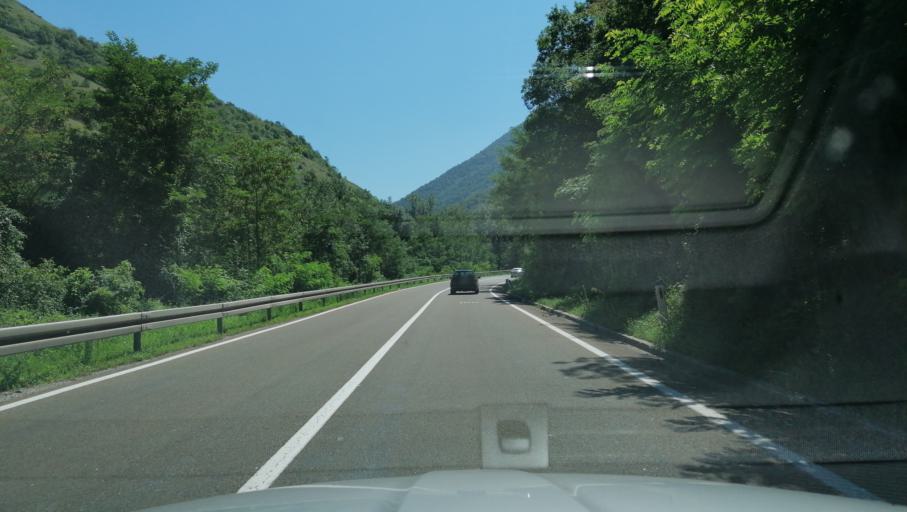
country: RS
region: Central Serbia
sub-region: Raski Okrug
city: Kraljevo
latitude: 43.5799
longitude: 20.5860
